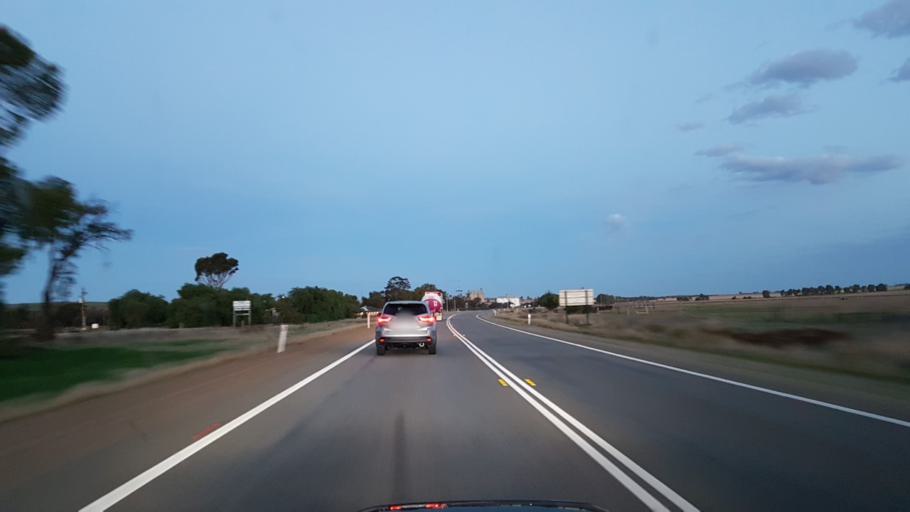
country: AU
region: South Australia
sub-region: Port Pirie City and Dists
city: Crystal Brook
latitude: -33.5353
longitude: 138.2132
